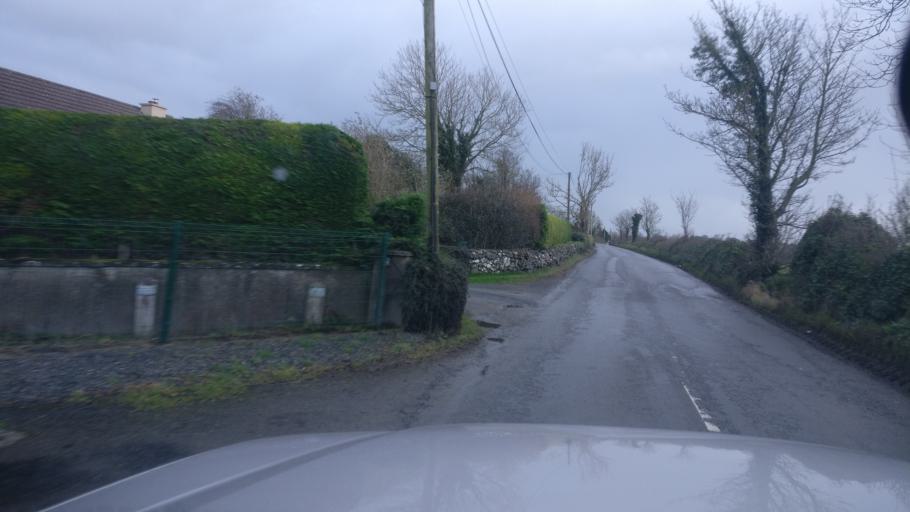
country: IE
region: Munster
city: Nenagh Bridge
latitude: 52.9831
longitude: -8.1012
